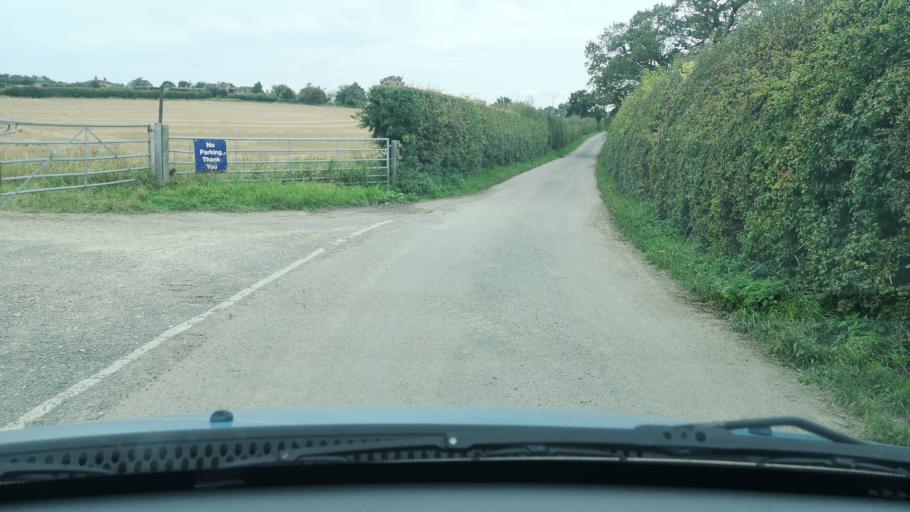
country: GB
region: England
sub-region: City and Borough of Wakefield
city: Featherstone
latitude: 53.6592
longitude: -1.3650
